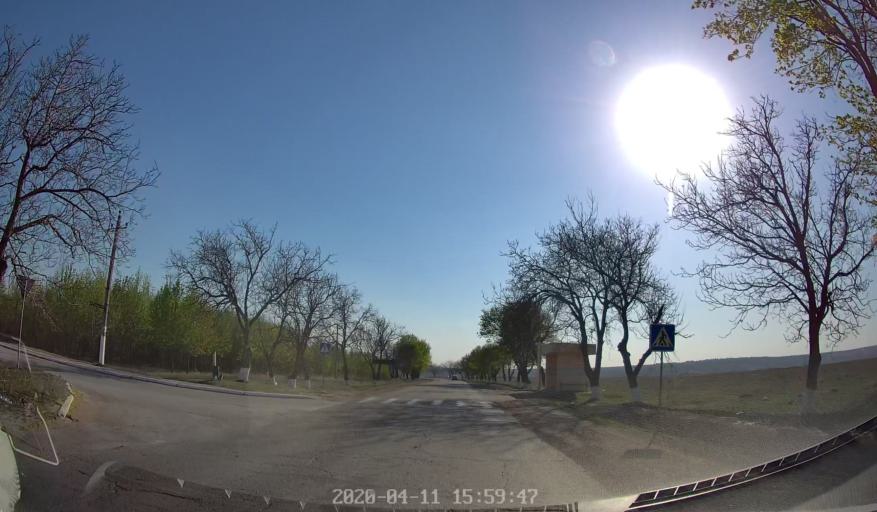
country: MD
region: Chisinau
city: Vadul lui Voda
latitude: 47.0800
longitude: 29.1385
